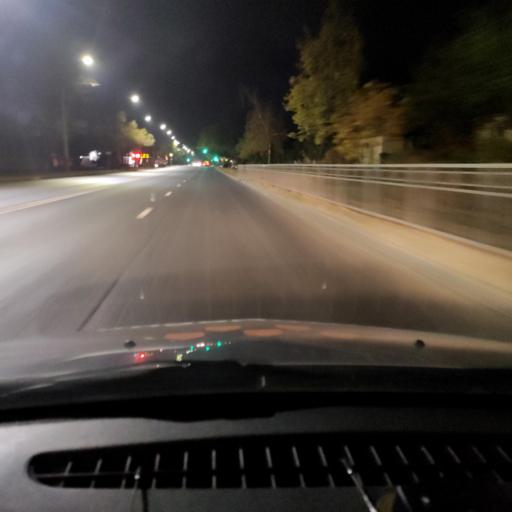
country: RU
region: Voronezj
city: Somovo
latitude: 51.7142
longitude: 39.2752
